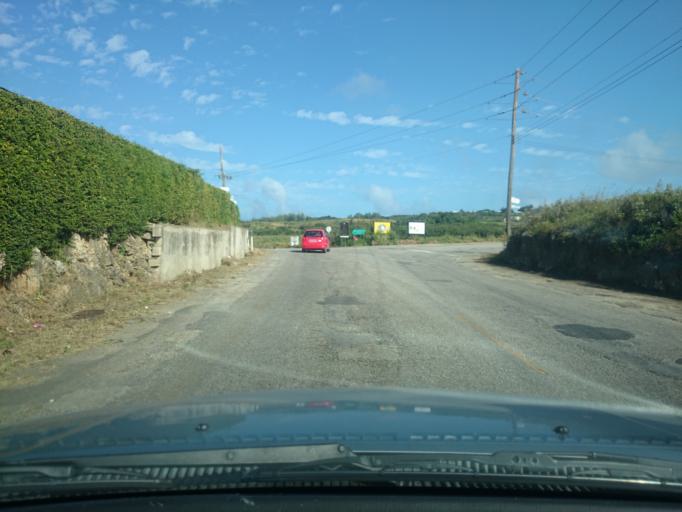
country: BB
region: Saint Lucy
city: Checker Hall
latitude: 13.2723
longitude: -59.6038
